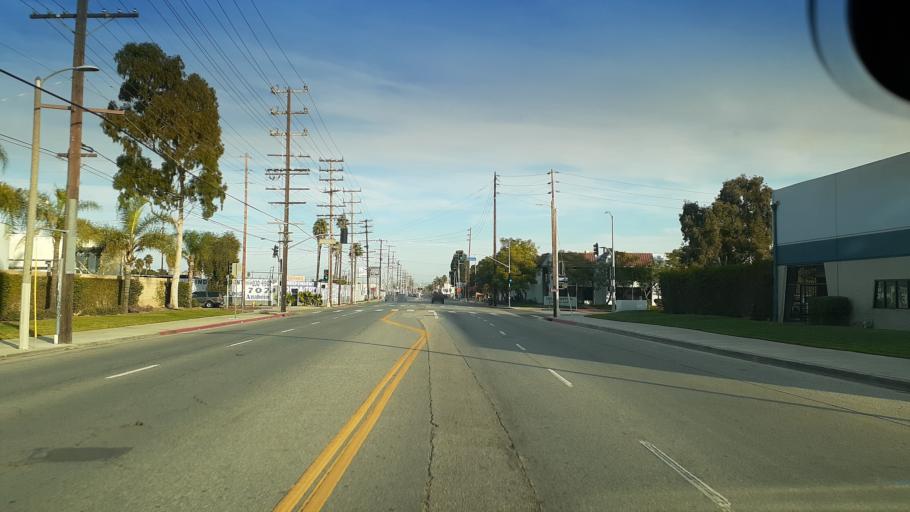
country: US
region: California
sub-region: Los Angeles County
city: West Carson
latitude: 33.7803
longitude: -118.2559
